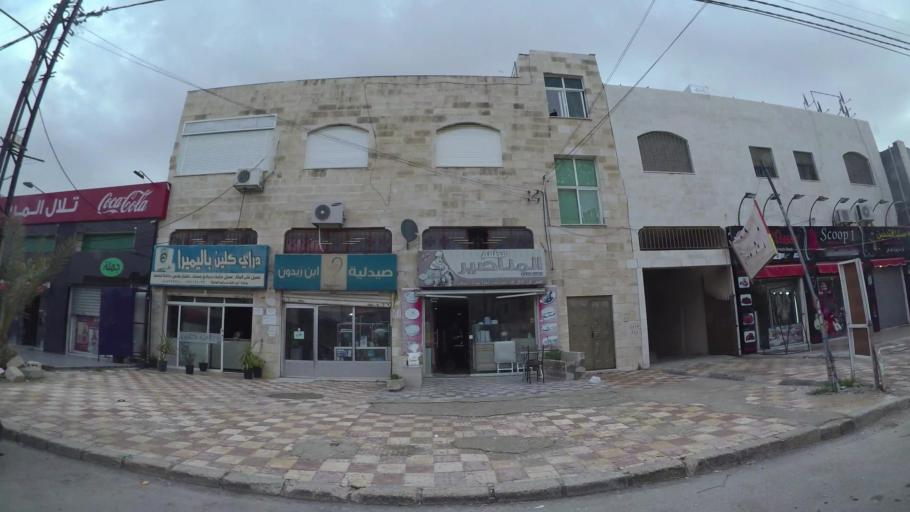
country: JO
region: Amman
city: Umm as Summaq
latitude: 31.9053
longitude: 35.8471
